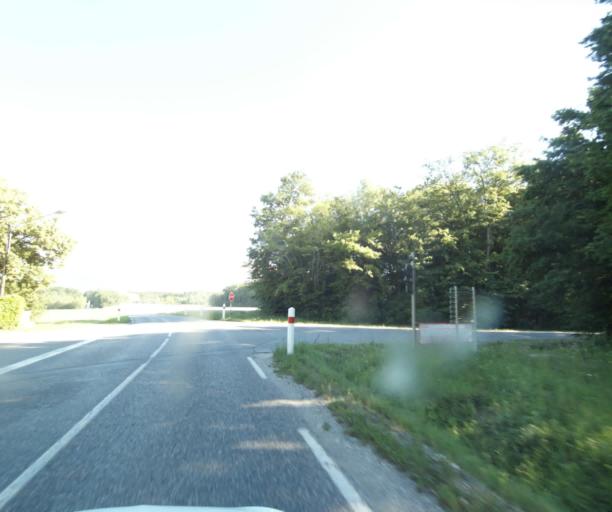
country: FR
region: Rhone-Alpes
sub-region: Departement de la Haute-Savoie
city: Douvaine
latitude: 46.3261
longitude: 6.2924
